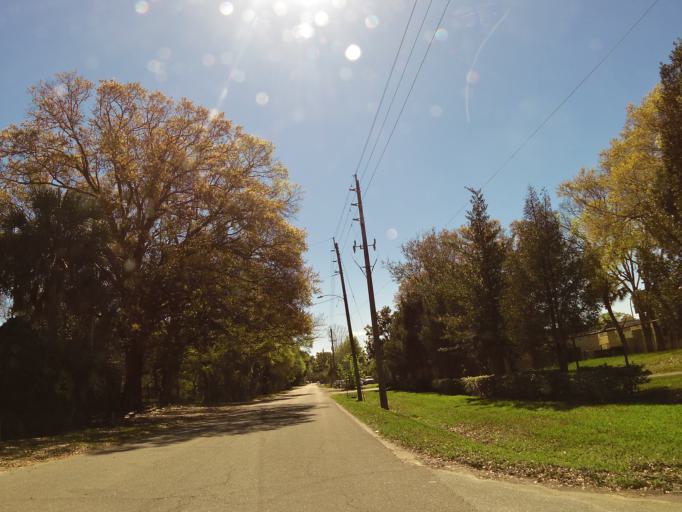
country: US
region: Florida
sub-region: Duval County
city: Jacksonville
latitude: 30.3263
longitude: -81.7175
